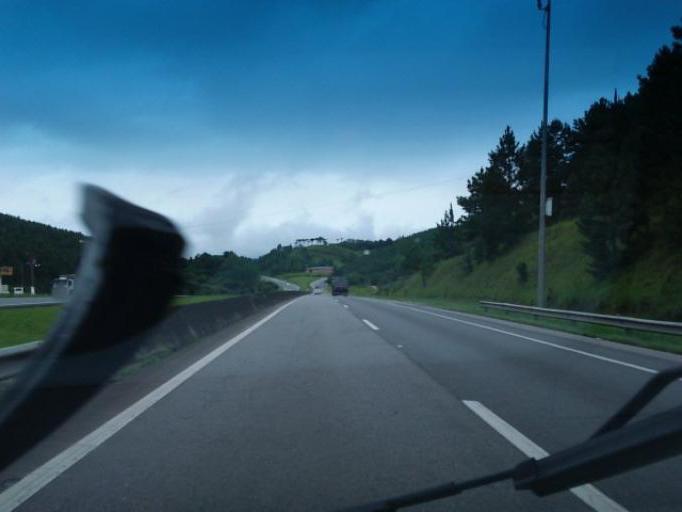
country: BR
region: Parana
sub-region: Campina Grande Do Sul
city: Campina Grande do Sul
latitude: -25.1215
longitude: -48.8555
